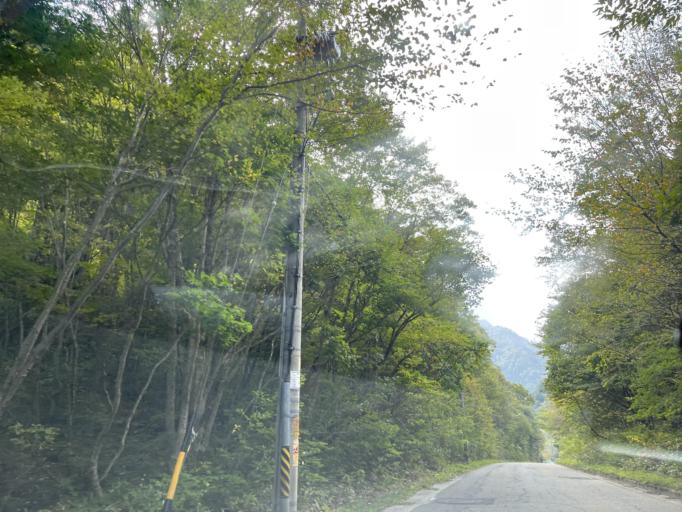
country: JP
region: Nagano
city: Omachi
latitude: 36.4977
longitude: 137.7563
